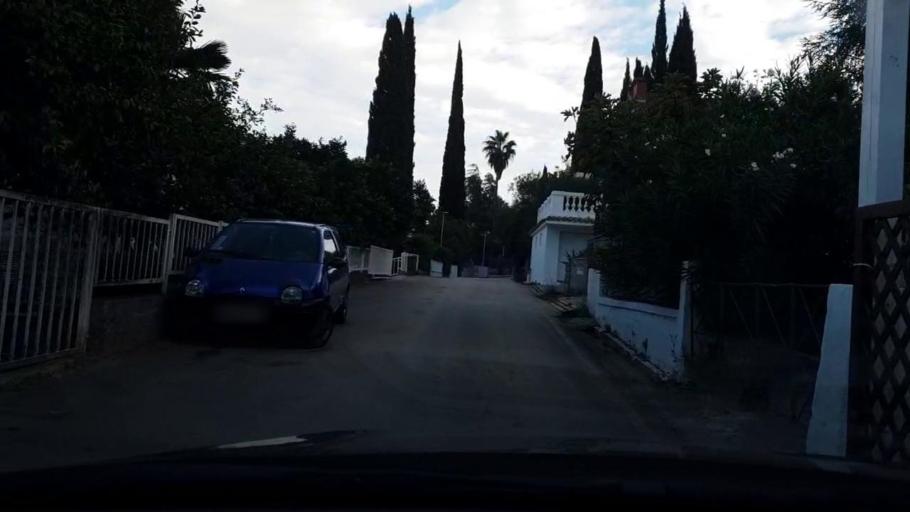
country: ME
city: Igalo
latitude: 42.4360
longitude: 18.5137
